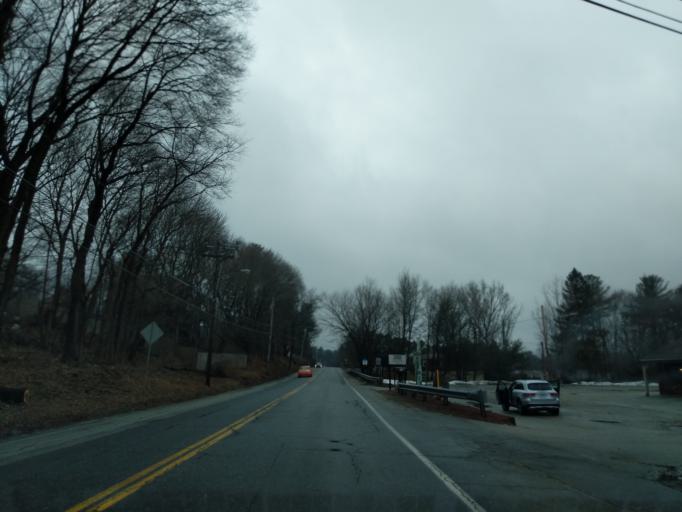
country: US
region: Massachusetts
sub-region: Worcester County
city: Webster
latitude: 42.0798
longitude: -71.8696
